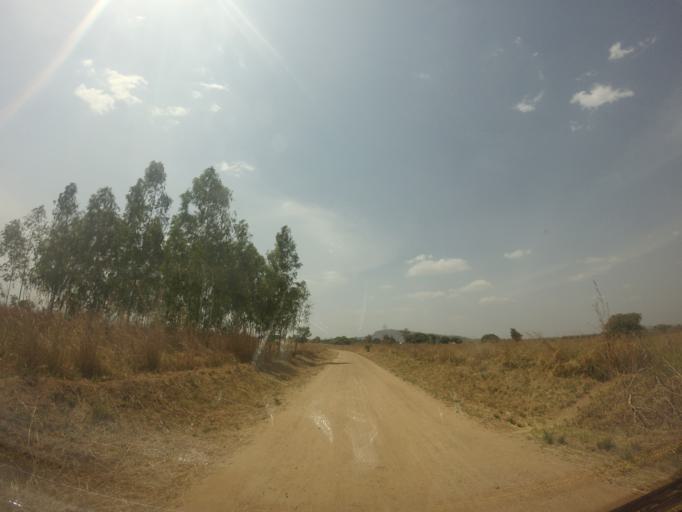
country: UG
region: Northern Region
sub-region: Arua District
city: Arua
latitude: 2.9113
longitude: 31.0502
